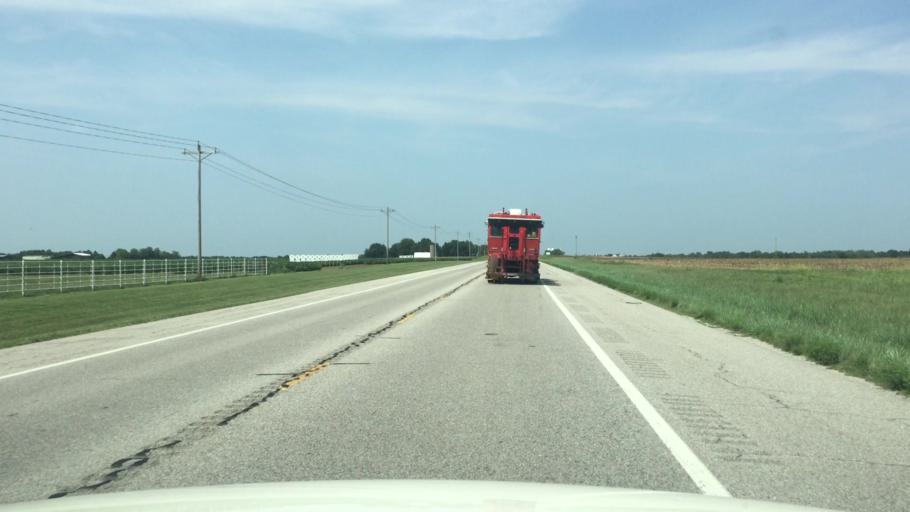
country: US
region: Missouri
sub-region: Jasper County
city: Carl Junction
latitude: 37.2260
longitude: -94.7049
